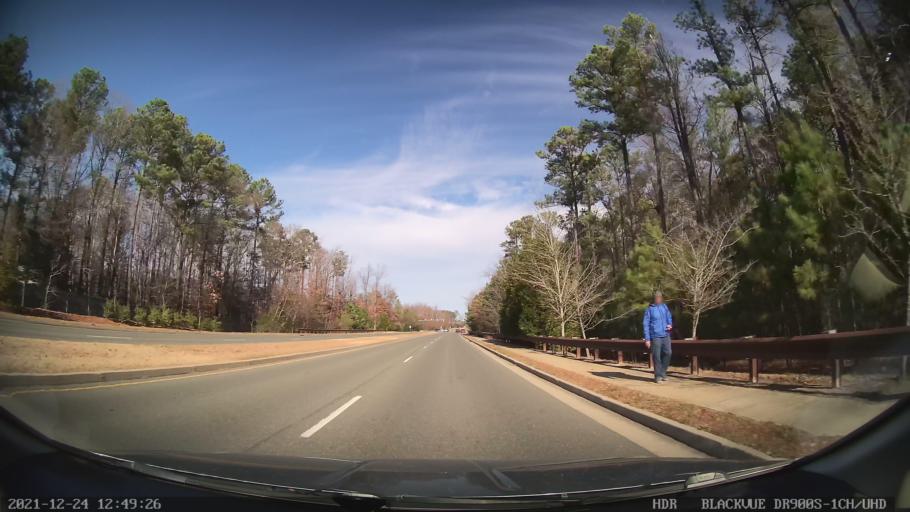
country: US
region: Virginia
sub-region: Henrico County
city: Short Pump
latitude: 37.6423
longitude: -77.6113
